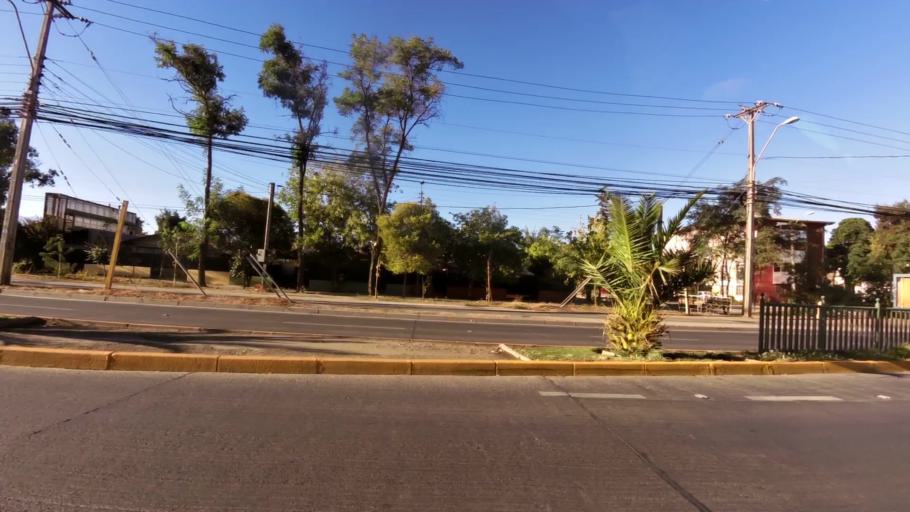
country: CL
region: O'Higgins
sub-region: Provincia de Cachapoal
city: Rancagua
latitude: -34.1738
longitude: -70.7171
